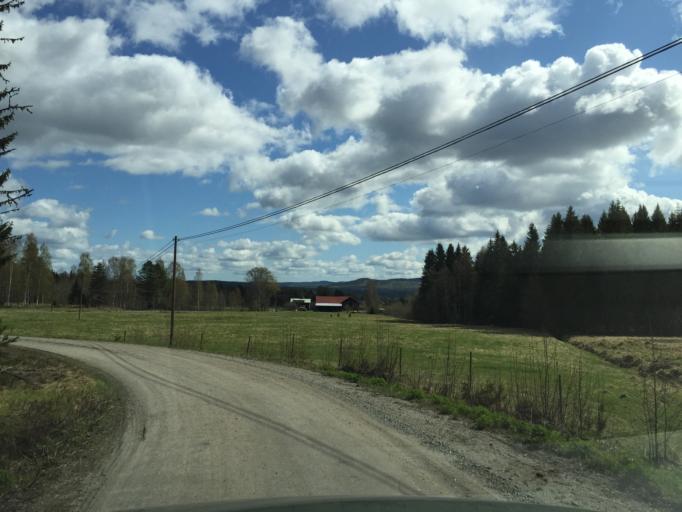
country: SE
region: Gaevleborg
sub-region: Bollnas Kommun
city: Arbra
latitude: 61.5226
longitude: 16.3194
